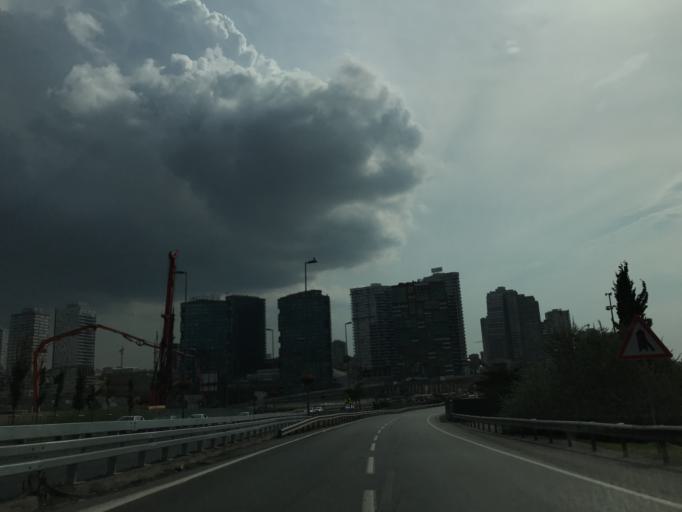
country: TR
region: Istanbul
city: UEskuedar
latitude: 41.0006
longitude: 29.0578
